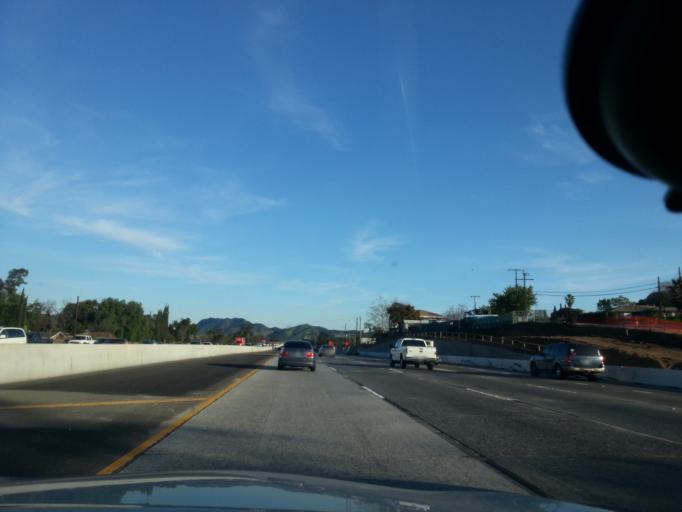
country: US
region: California
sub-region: Ventura County
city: Thousand Oaks
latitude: 34.1687
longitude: -118.8420
